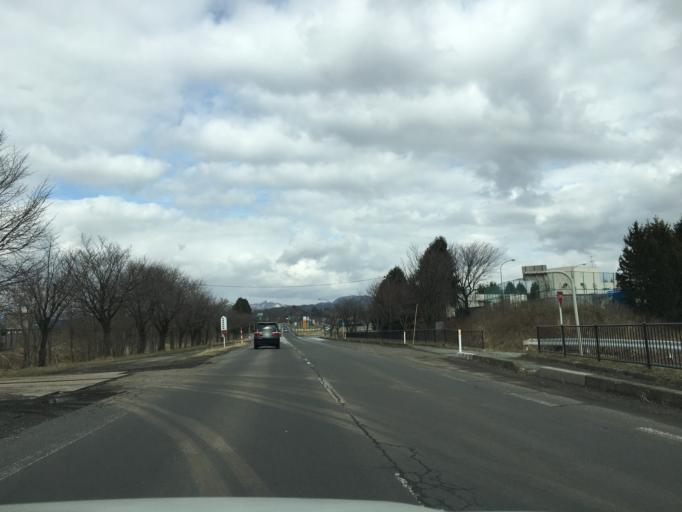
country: JP
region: Akita
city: Hanawa
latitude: 40.2548
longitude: 140.7605
